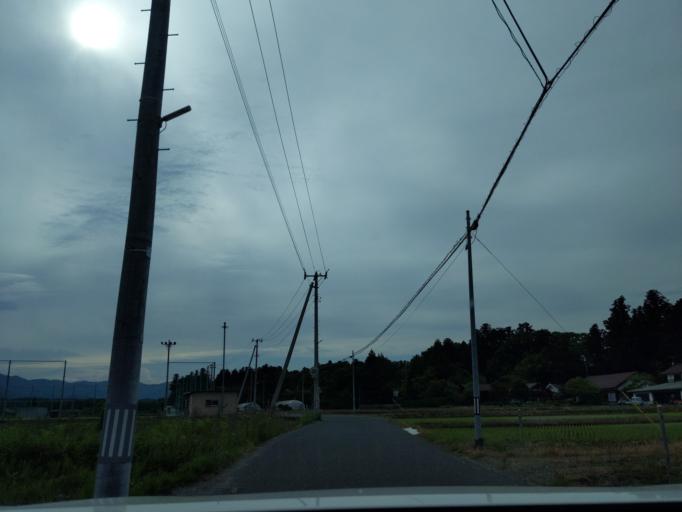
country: JP
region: Fukushima
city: Koriyama
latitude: 37.3785
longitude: 140.3103
